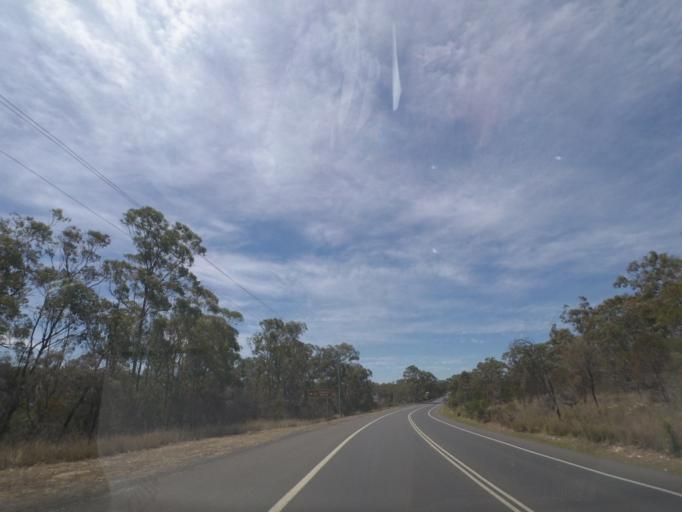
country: AU
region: New South Wales
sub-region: Wollondilly
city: Buxton
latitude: -34.2394
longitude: 150.5785
